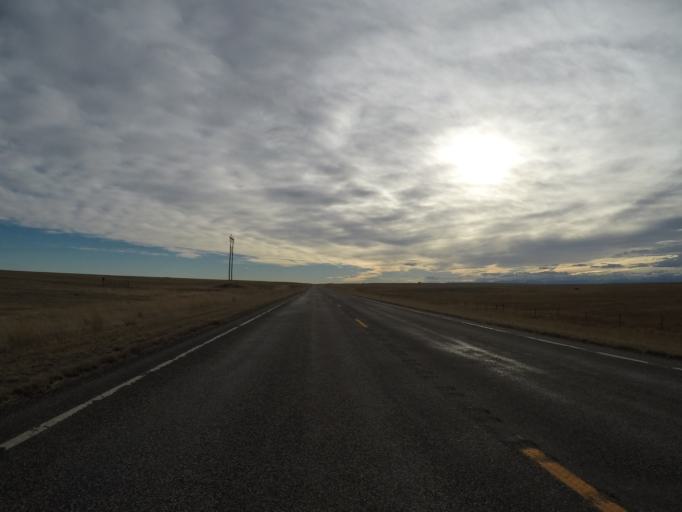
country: US
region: Montana
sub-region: Yellowstone County
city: Laurel
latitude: 45.8503
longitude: -108.8812
